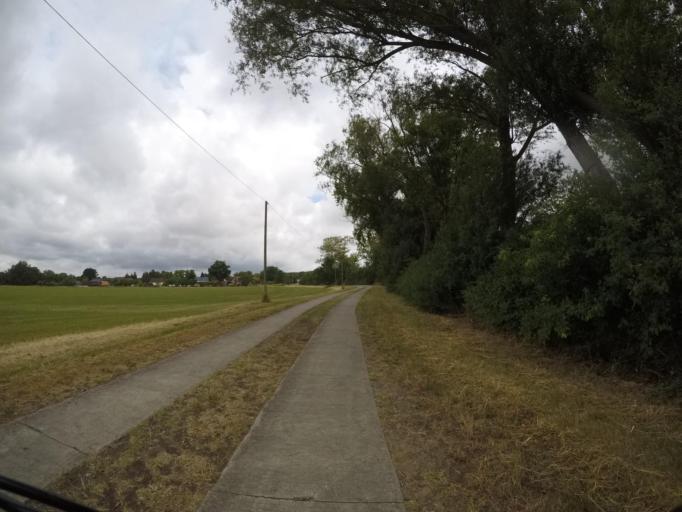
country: DE
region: Lower Saxony
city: Hitzacker
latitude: 53.1790
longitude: 11.1102
